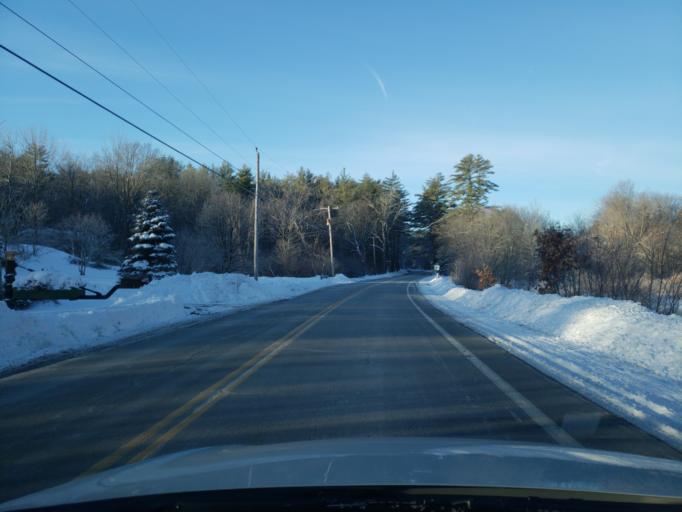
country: US
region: New Hampshire
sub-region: Hillsborough County
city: Goffstown
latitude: 43.0162
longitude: -71.6269
